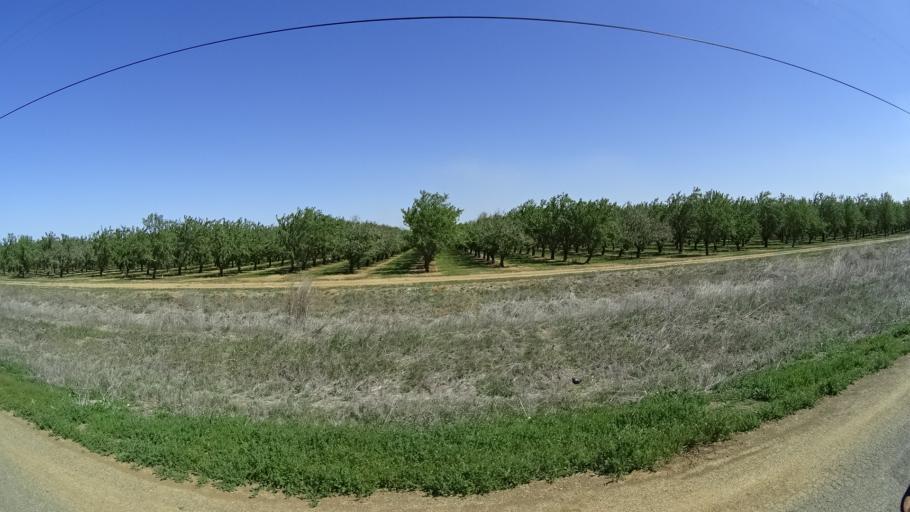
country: US
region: California
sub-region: Glenn County
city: Willows
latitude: 39.4963
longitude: -122.2773
